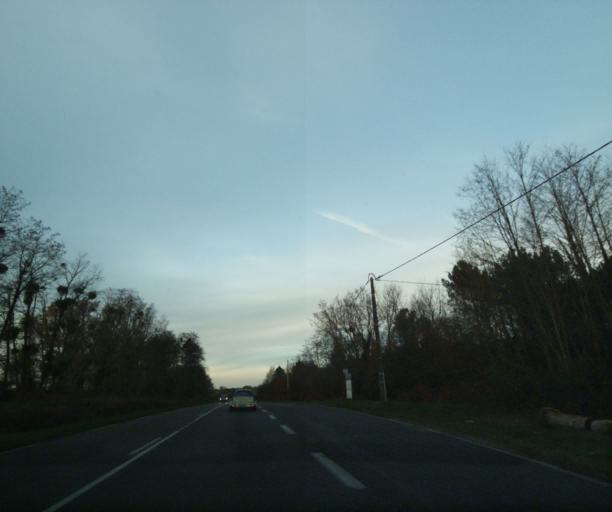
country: FR
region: Aquitaine
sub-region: Departement de la Gironde
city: Langon
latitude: 44.4957
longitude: -0.2364
